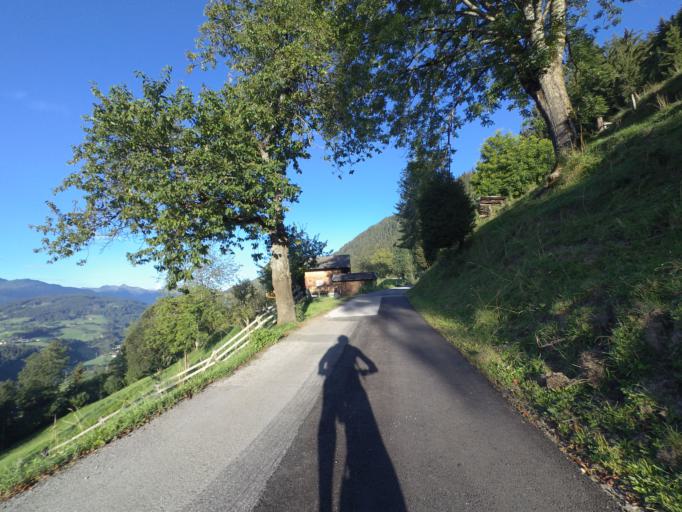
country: AT
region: Salzburg
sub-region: Politischer Bezirk Sankt Johann im Pongau
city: Goldegg
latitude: 47.3392
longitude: 13.0995
